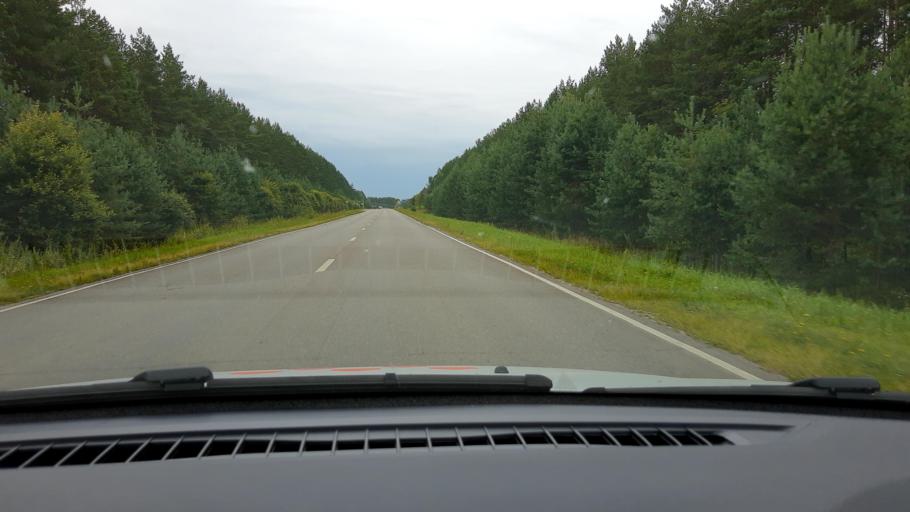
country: RU
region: Nizjnij Novgorod
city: Vyyezdnoye
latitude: 55.1994
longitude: 43.6207
